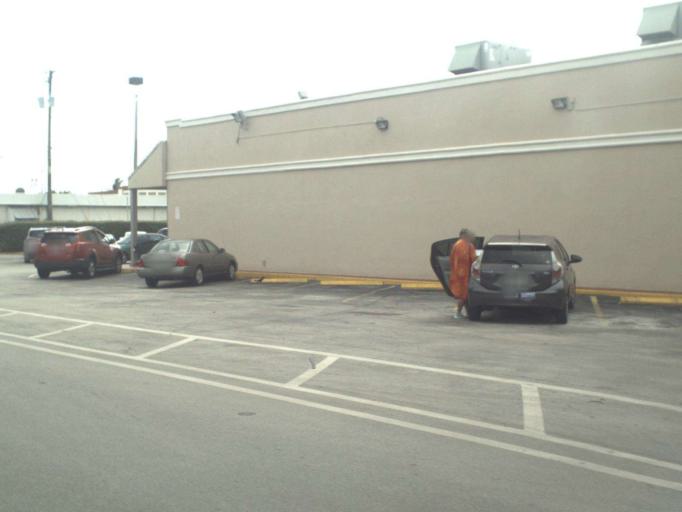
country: US
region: Florida
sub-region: Miami-Dade County
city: Coral Terrace
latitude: 25.7351
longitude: -80.2866
